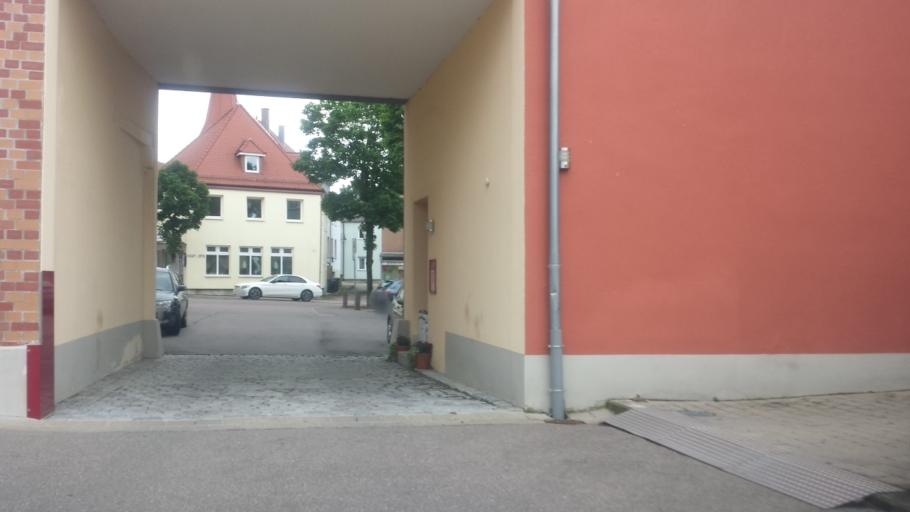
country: DE
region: Baden-Wuerttemberg
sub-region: Regierungsbezirk Stuttgart
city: Ilshofen
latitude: 49.1696
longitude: 9.9189
